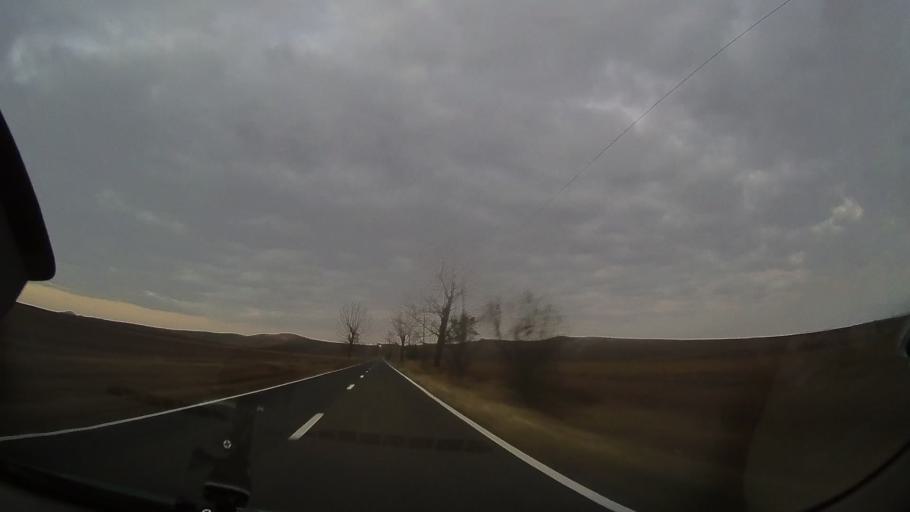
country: RO
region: Tulcea
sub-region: Comuna Nalbant
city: Nicolae Balcescu
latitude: 45.0073
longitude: 28.5980
